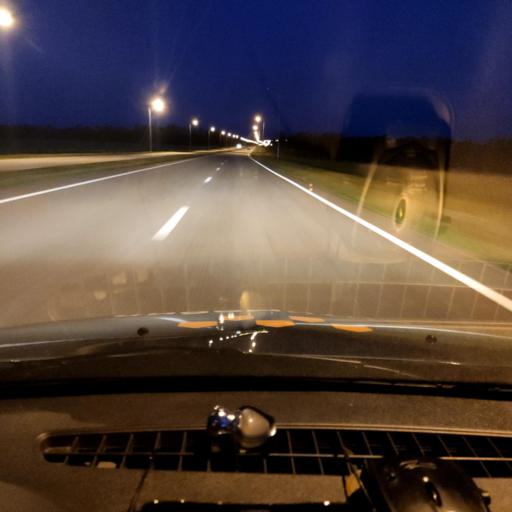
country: RU
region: Belgorod
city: Skorodnoye
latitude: 51.0294
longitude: 37.2062
